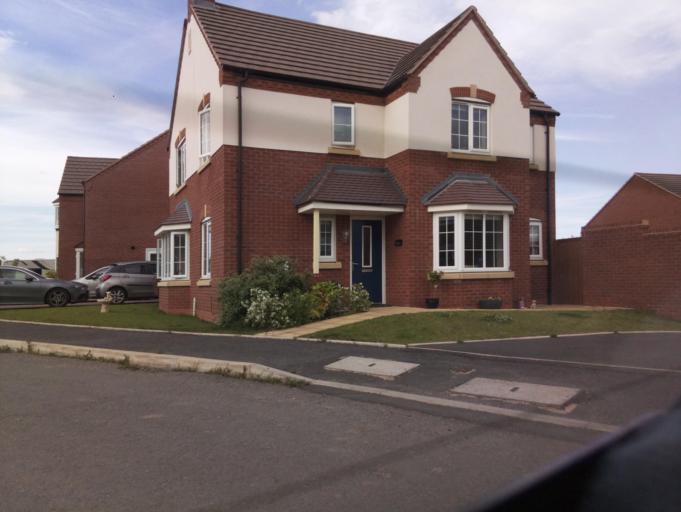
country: GB
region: England
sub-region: Worcestershire
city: Evesham
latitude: 52.0868
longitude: -1.9689
